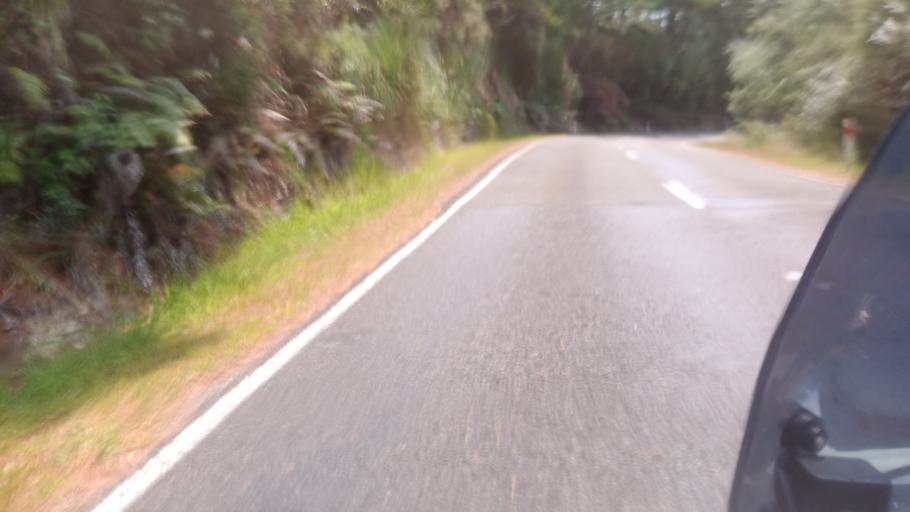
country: NZ
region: Bay of Plenty
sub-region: Opotiki District
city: Opotiki
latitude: -37.5790
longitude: 178.1178
